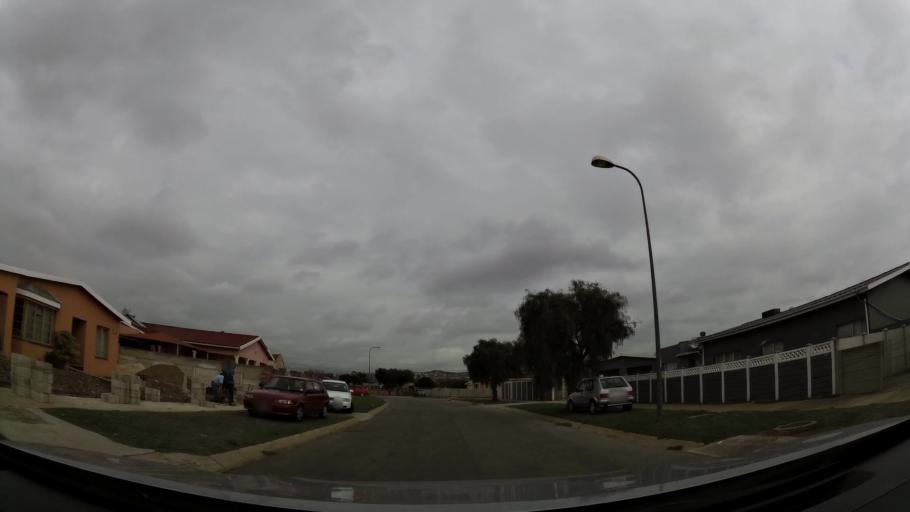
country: ZA
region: Eastern Cape
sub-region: Nelson Mandela Bay Metropolitan Municipality
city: Port Elizabeth
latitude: -33.8987
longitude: 25.5528
